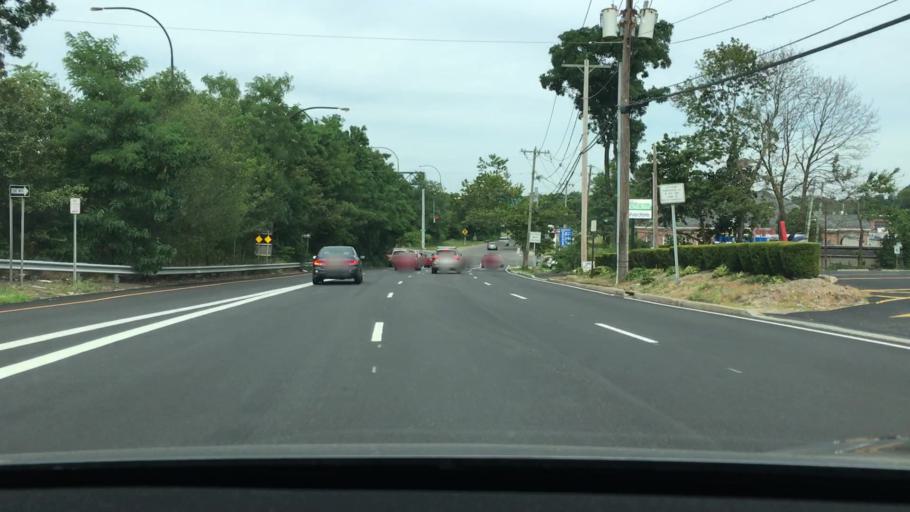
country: US
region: New York
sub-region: Nassau County
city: Roslyn Heights
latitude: 40.7844
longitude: -73.6505
